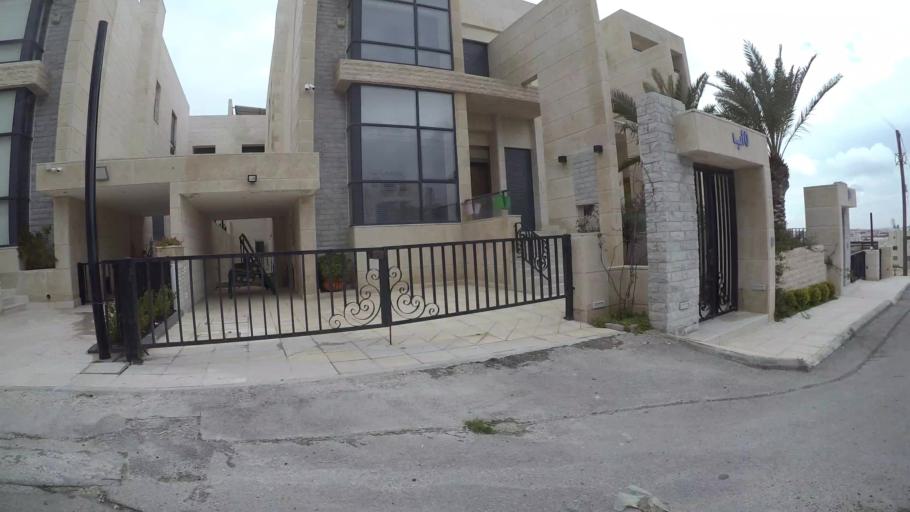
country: JO
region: Amman
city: Al Jubayhah
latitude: 31.9935
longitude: 35.8358
